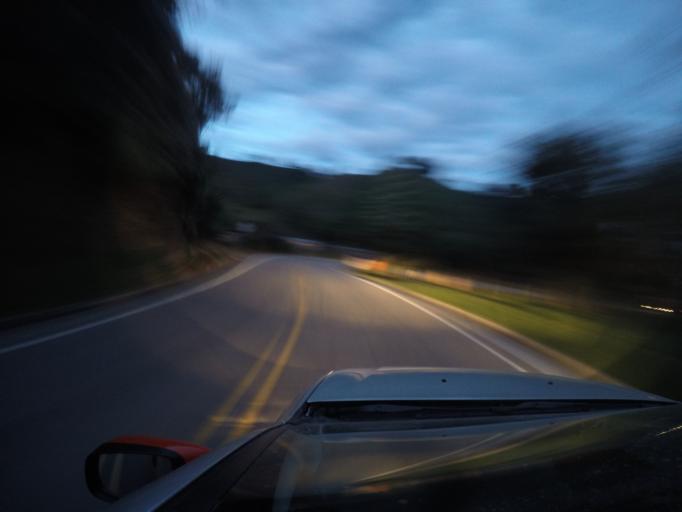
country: CO
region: Tolima
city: Casabianca
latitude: 5.1416
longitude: -75.1184
